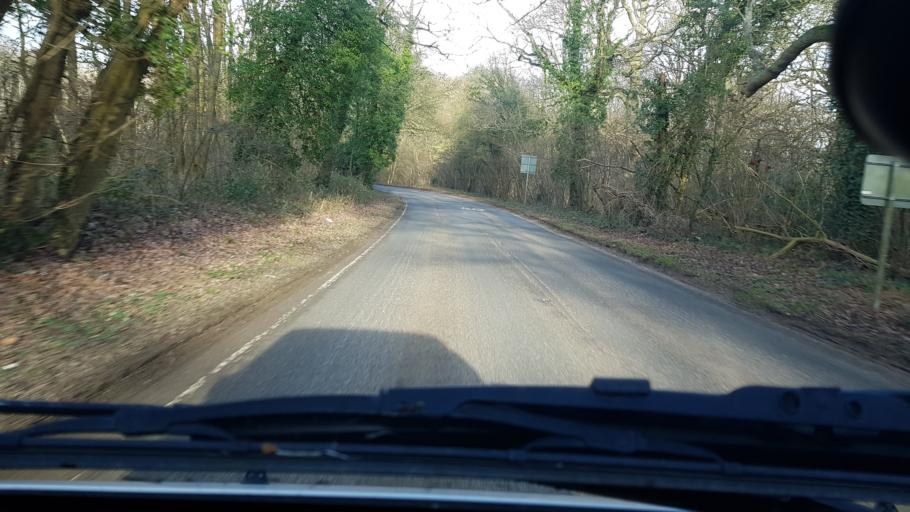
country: GB
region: England
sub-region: Surrey
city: Normandy
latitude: 51.2331
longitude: -0.6697
